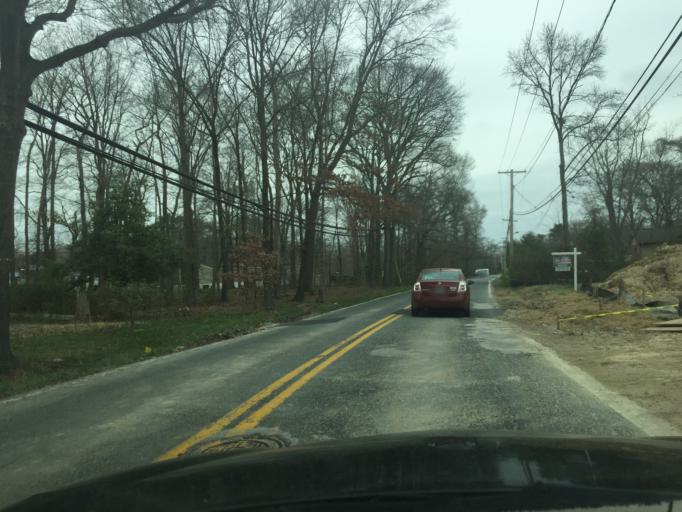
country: US
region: Maryland
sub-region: Baltimore County
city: Bowleys Quarters
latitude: 39.3402
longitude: -76.3968
